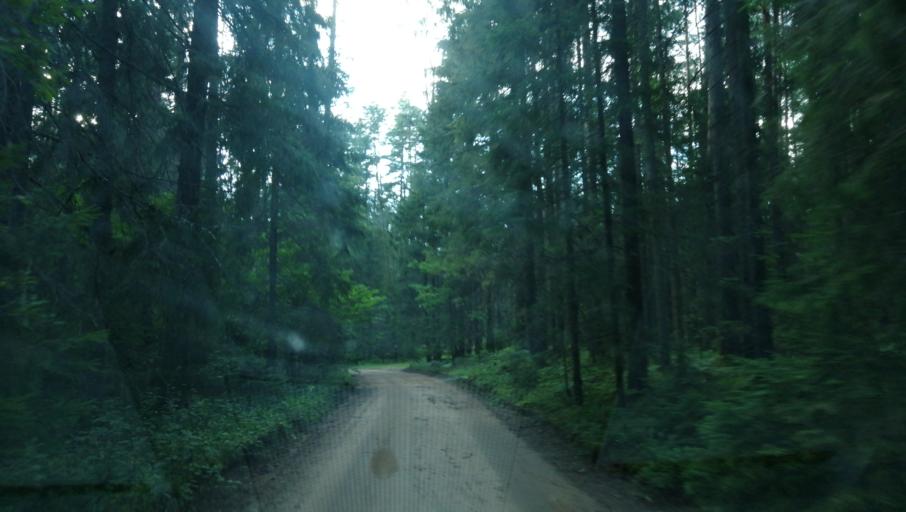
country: LV
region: Cesu Rajons
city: Cesis
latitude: 57.2897
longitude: 25.1962
